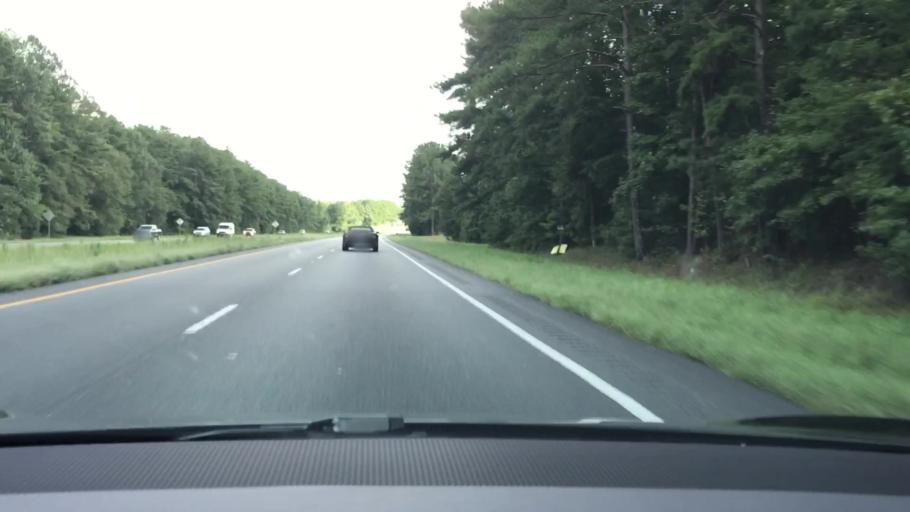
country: US
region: Alabama
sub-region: Pike County
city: Troy
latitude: 31.9148
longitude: -86.0139
